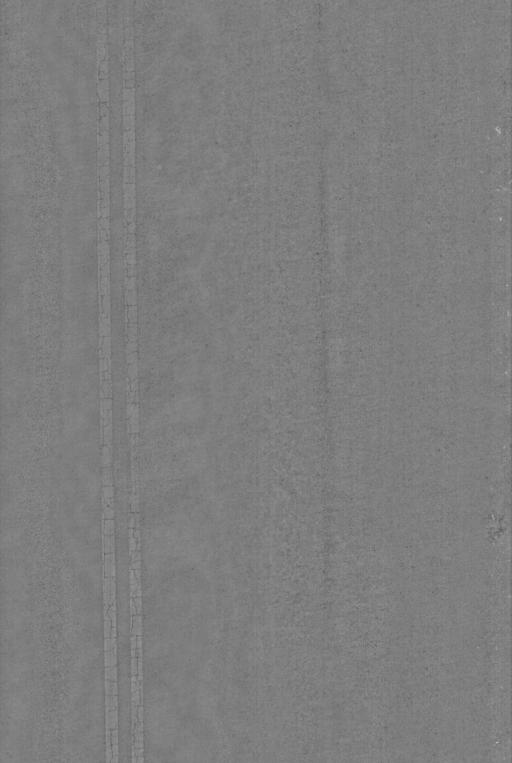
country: US
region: Maryland
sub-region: Prince George's County
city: Mount Rainier
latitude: 38.9273
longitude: -76.9608
